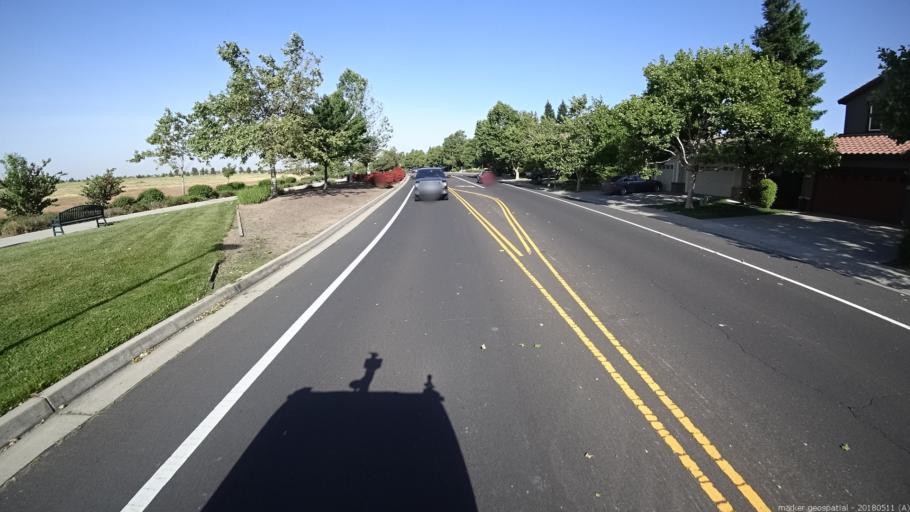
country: US
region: California
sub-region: Sacramento County
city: Elverta
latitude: 38.6663
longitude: -121.5163
